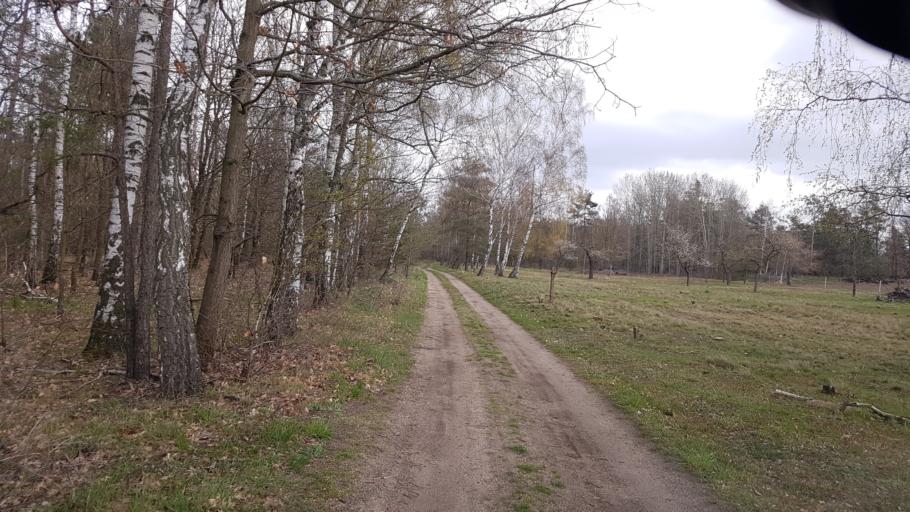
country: DE
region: Brandenburg
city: Hohenleipisch
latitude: 51.5066
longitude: 13.5472
